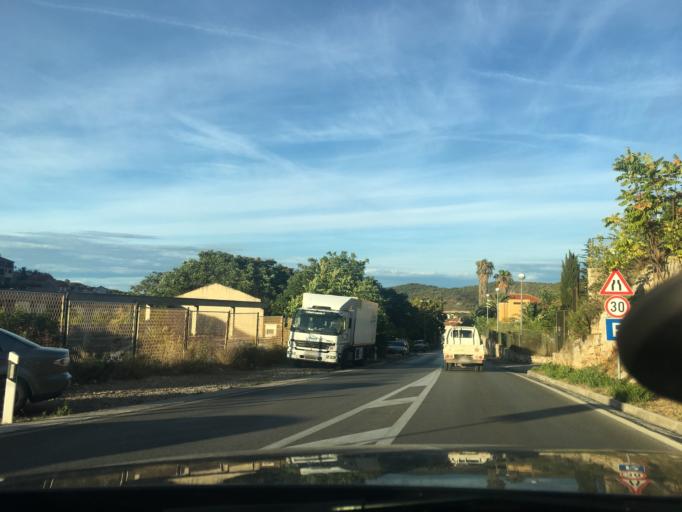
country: HR
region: Splitsko-Dalmatinska
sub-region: Grad Vis
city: Vis
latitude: 43.0592
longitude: 16.1798
